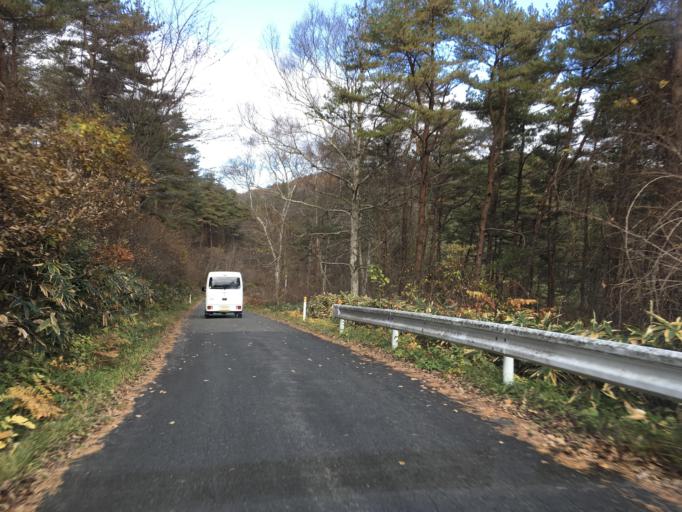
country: JP
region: Iwate
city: Mizusawa
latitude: 39.1269
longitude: 141.3058
